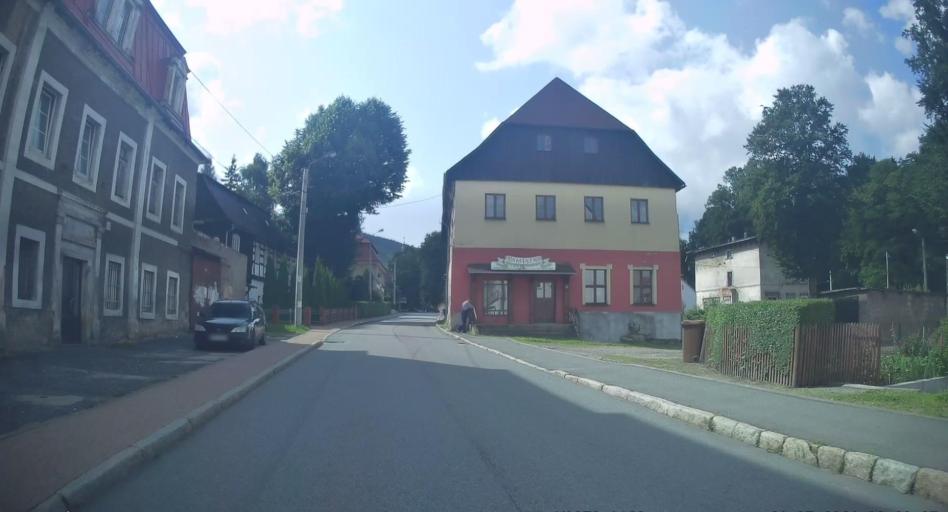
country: PL
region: Lower Silesian Voivodeship
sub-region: Powiat walbrzyski
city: Walim
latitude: 50.6996
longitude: 16.4409
